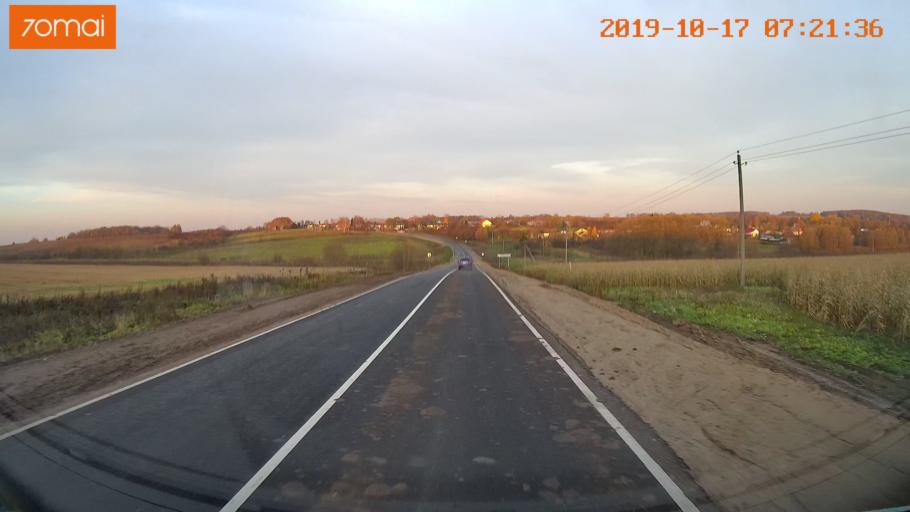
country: RU
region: Ivanovo
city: Gavrilov Posad
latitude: 56.3467
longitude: 40.1571
